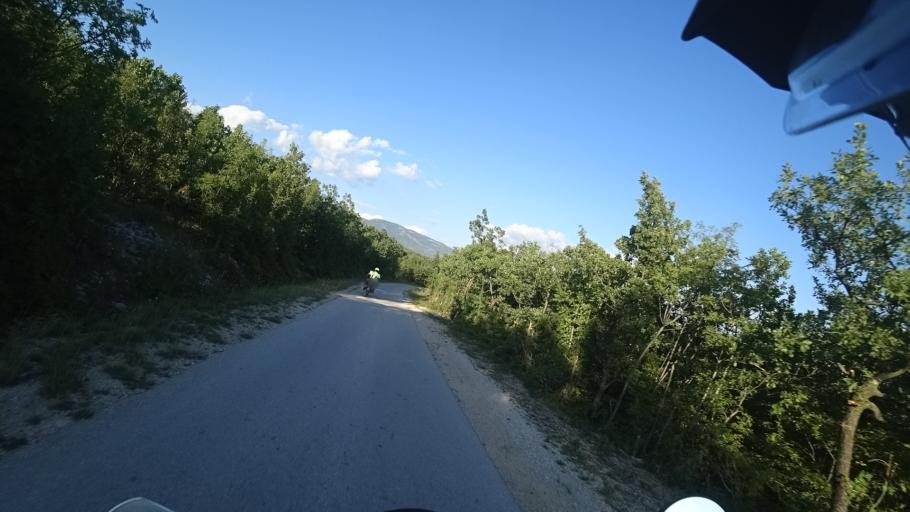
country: HR
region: Sibensko-Kniniska
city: Knin
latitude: 44.0638
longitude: 16.1698
